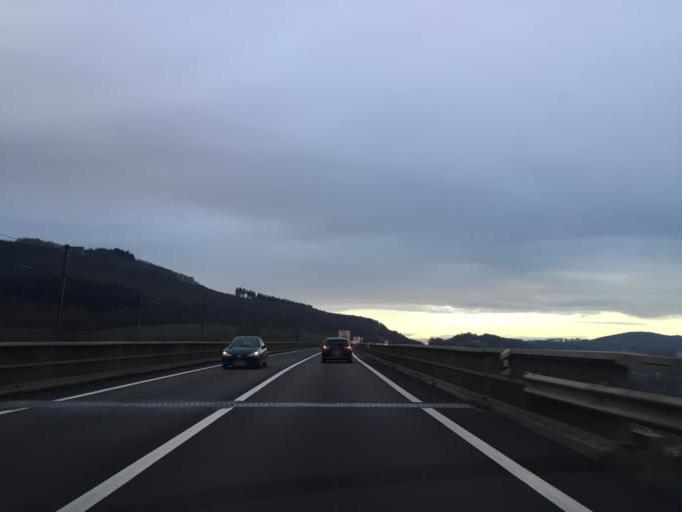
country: FR
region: Bourgogne
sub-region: Departement de Saone-et-Loire
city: La Roche-Vineuse
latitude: 46.3699
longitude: 4.6770
